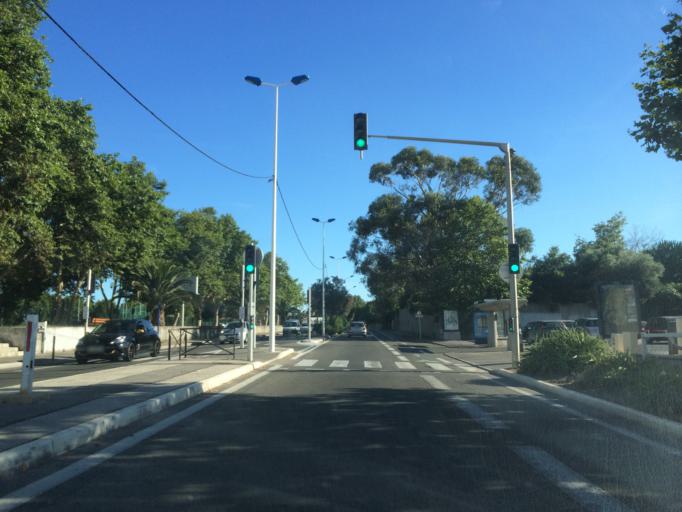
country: FR
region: Provence-Alpes-Cote d'Azur
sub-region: Departement des Alpes-Maritimes
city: Antibes
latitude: 43.5927
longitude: 7.1251
